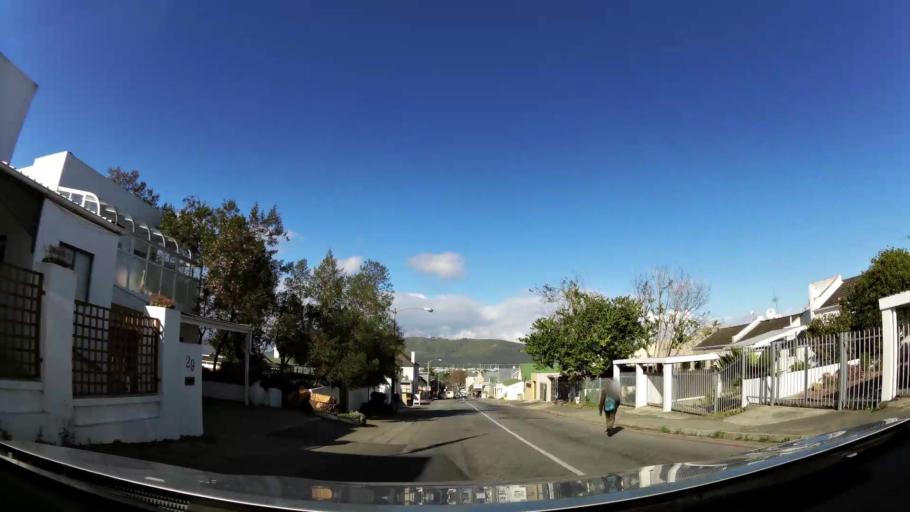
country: ZA
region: Western Cape
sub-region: Eden District Municipality
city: Knysna
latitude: -34.0336
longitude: 23.0468
